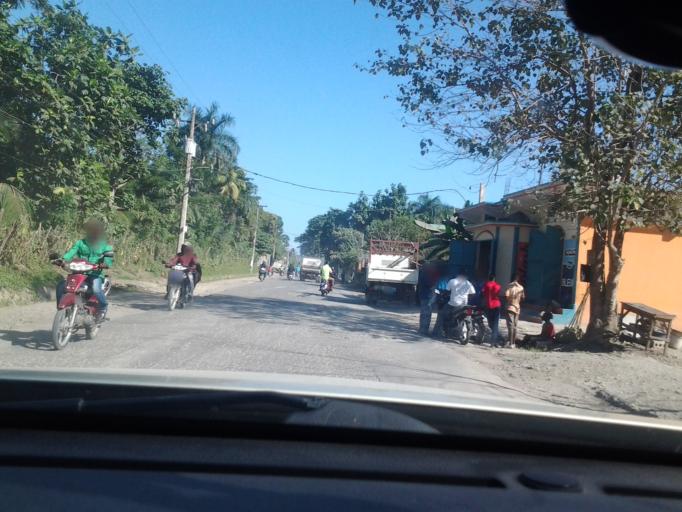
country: HT
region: Sud-Est
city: Jacmel
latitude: 18.2351
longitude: -72.5159
